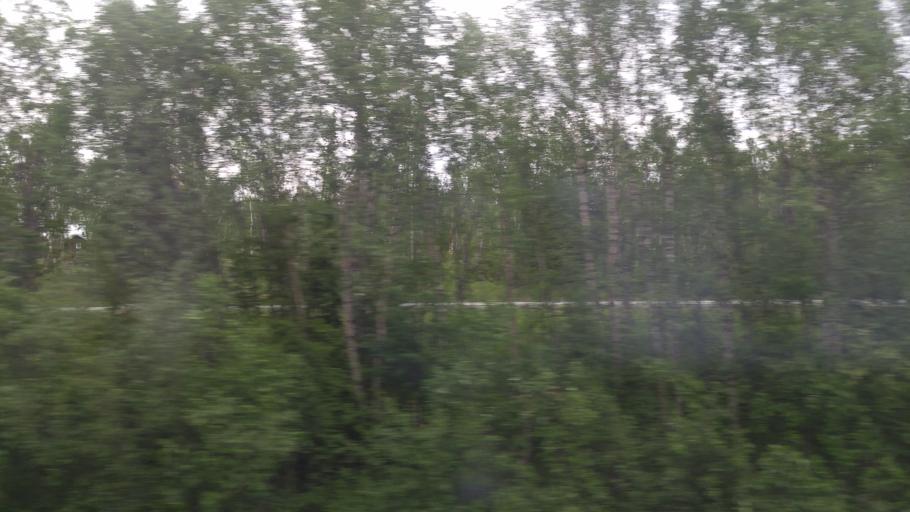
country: SE
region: Jaemtland
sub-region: Are Kommun
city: Are
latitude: 63.3618
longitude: 12.6419
